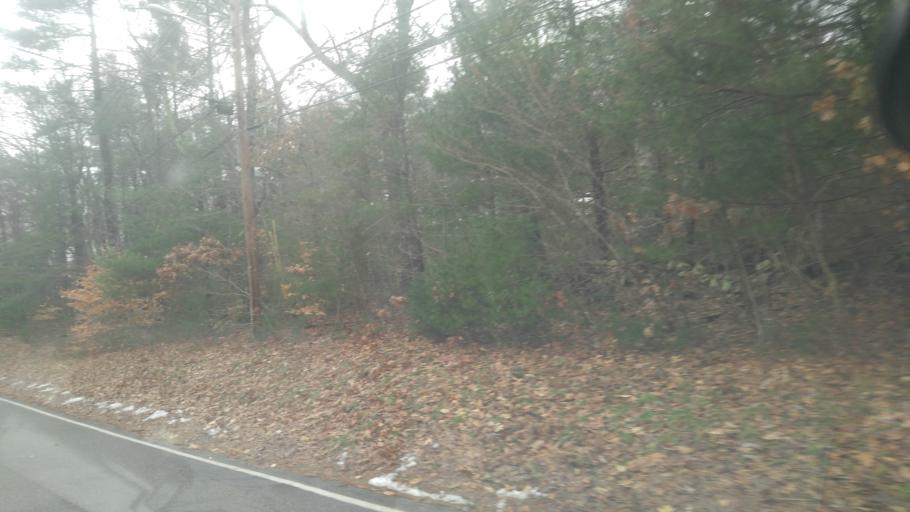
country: US
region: Rhode Island
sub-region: Kent County
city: West Warwick
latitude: 41.6458
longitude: -71.5413
